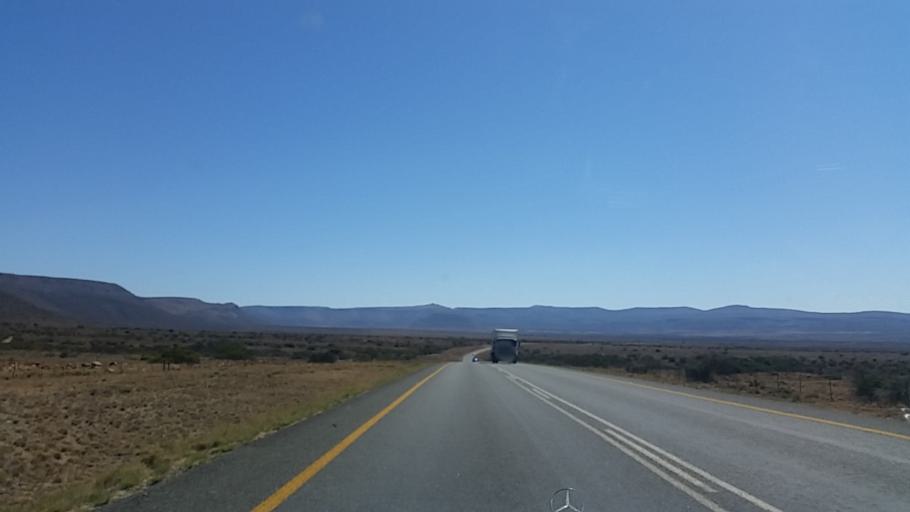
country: ZA
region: Eastern Cape
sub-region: Cacadu District Municipality
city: Graaff-Reinet
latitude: -32.0467
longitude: 24.6172
